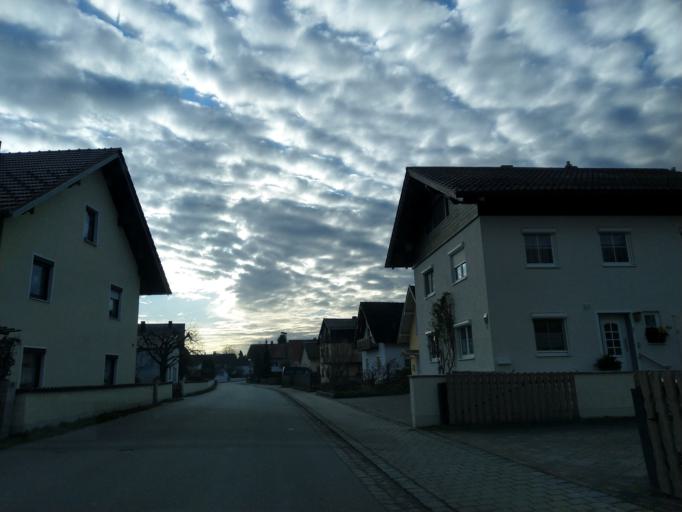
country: DE
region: Bavaria
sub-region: Lower Bavaria
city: Aholming
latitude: 48.7387
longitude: 12.9098
